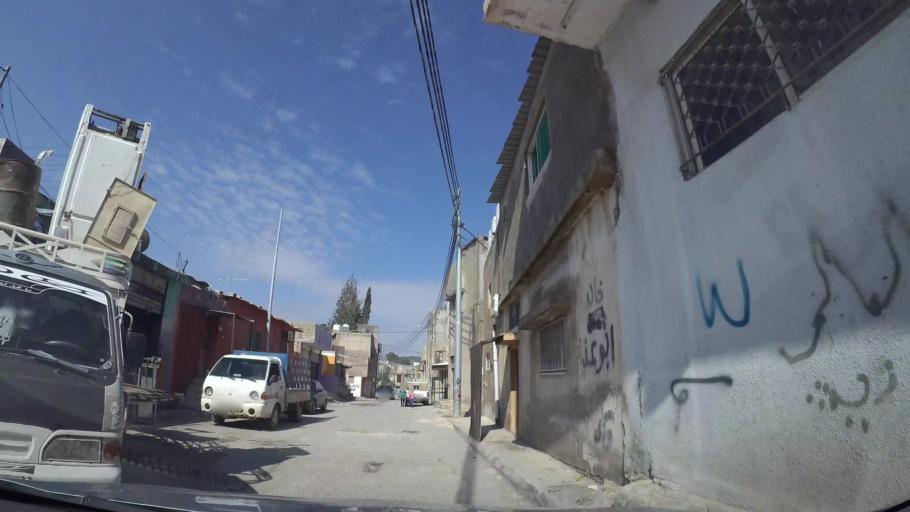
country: JO
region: Amman
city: Al Jubayhah
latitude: 32.0768
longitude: 35.8476
